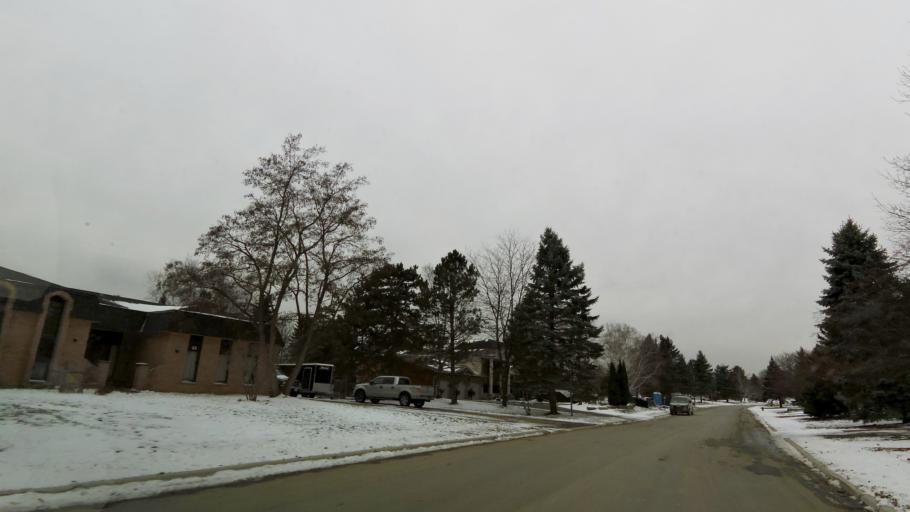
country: CA
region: Ontario
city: Vaughan
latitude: 43.8987
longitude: -79.6545
